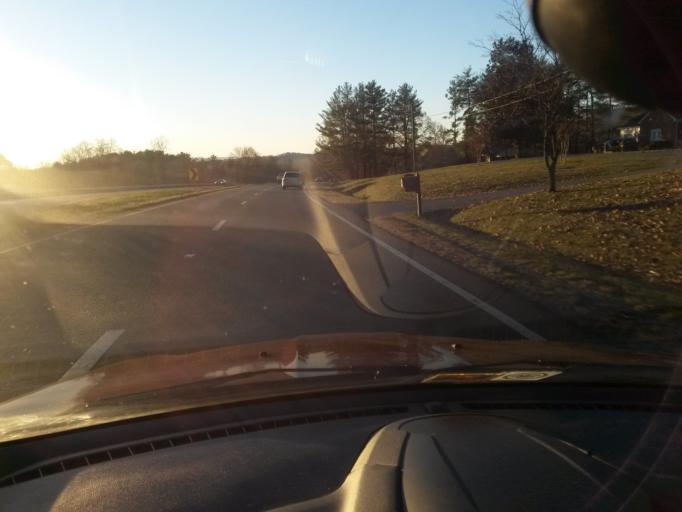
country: US
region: Virginia
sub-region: Franklin County
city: Rocky Mount
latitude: 37.0643
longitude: -79.8859
